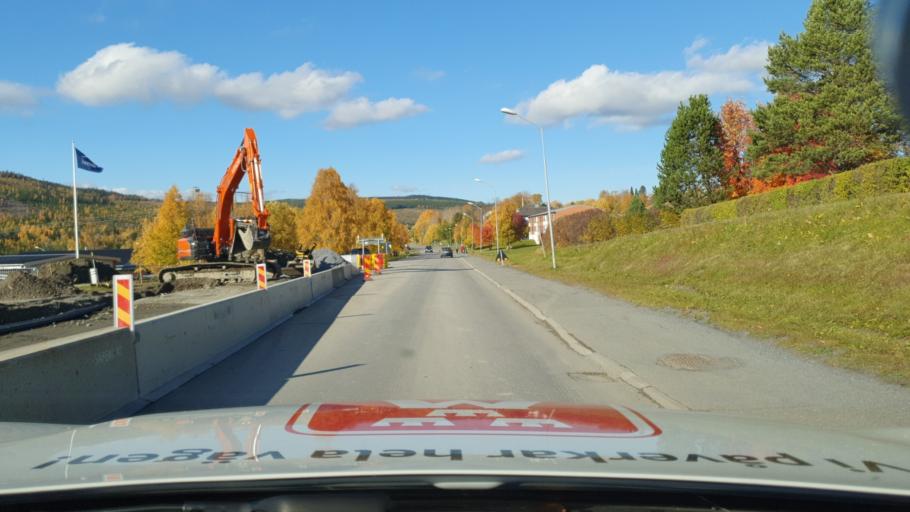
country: SE
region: Jaemtland
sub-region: Are Kommun
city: Jarpen
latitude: 63.3503
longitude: 13.4516
